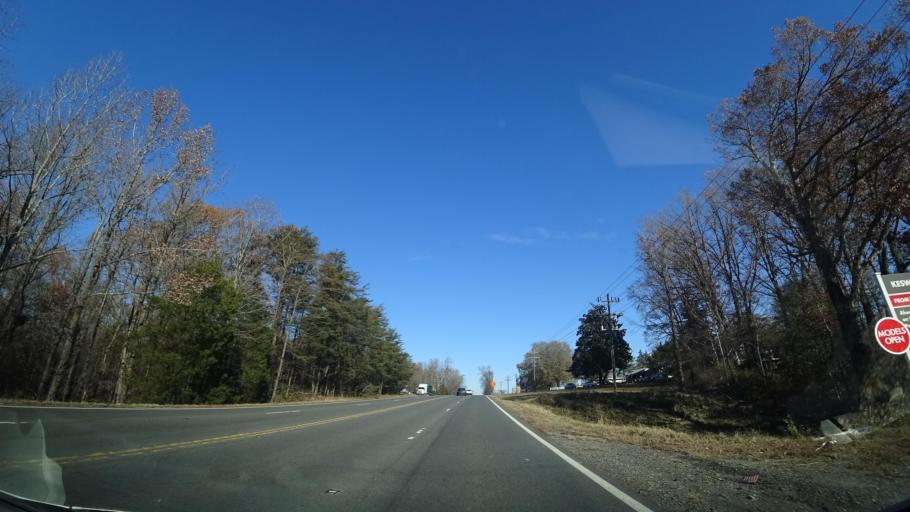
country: US
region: Virginia
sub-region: Spotsylvania County
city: Spotsylvania Courthouse
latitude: 38.2097
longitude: -77.5076
